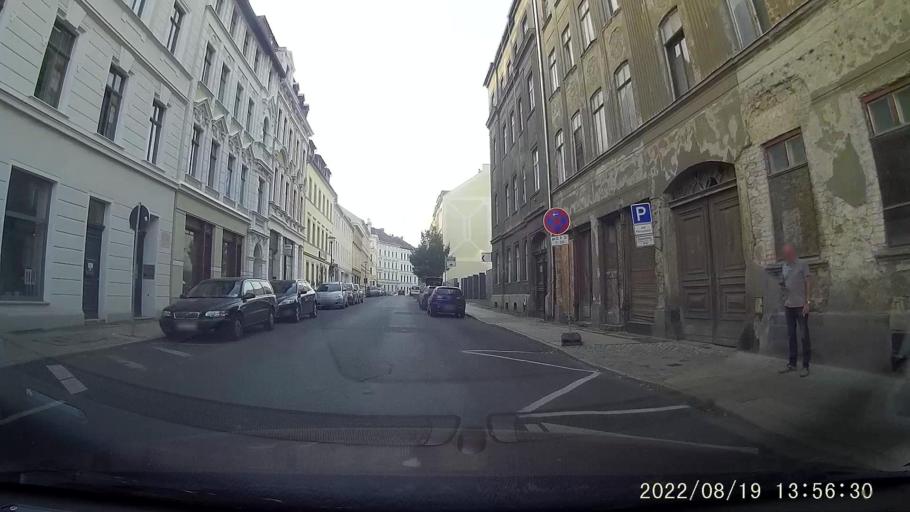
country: DE
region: Saxony
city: Goerlitz
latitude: 51.1562
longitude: 14.9638
